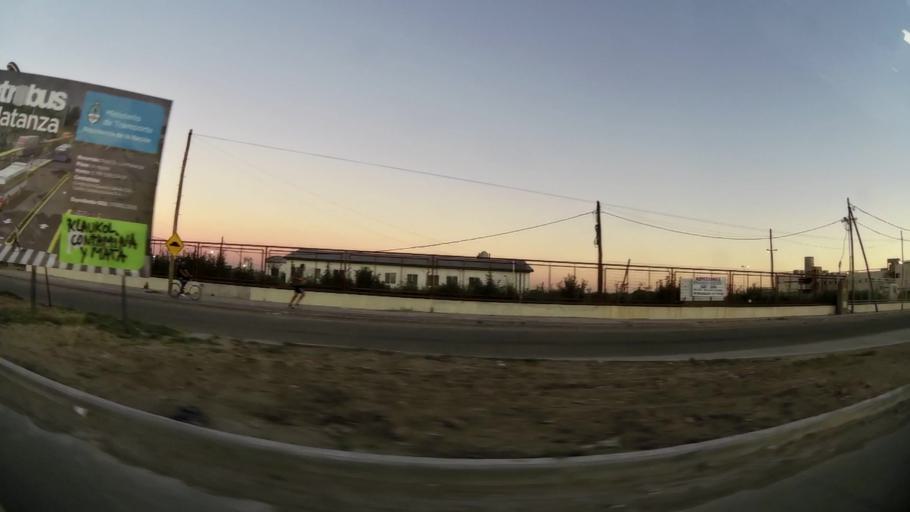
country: AR
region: Buenos Aires
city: San Justo
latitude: -34.7291
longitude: -58.6007
